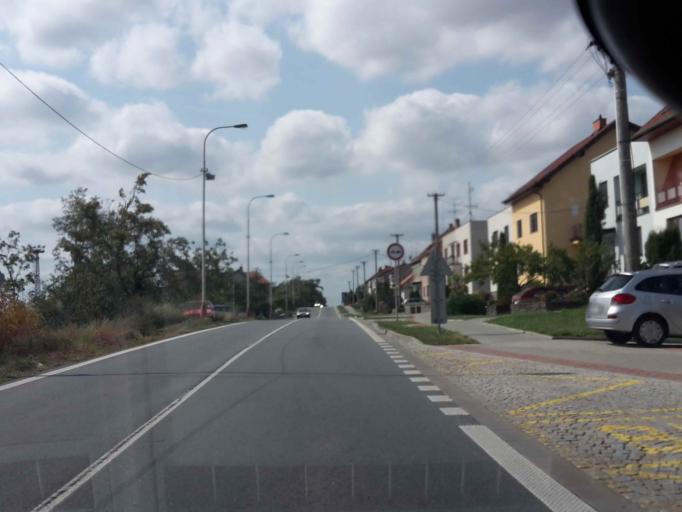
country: CZ
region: South Moravian
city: Rousinov
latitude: 49.1992
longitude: 16.8711
